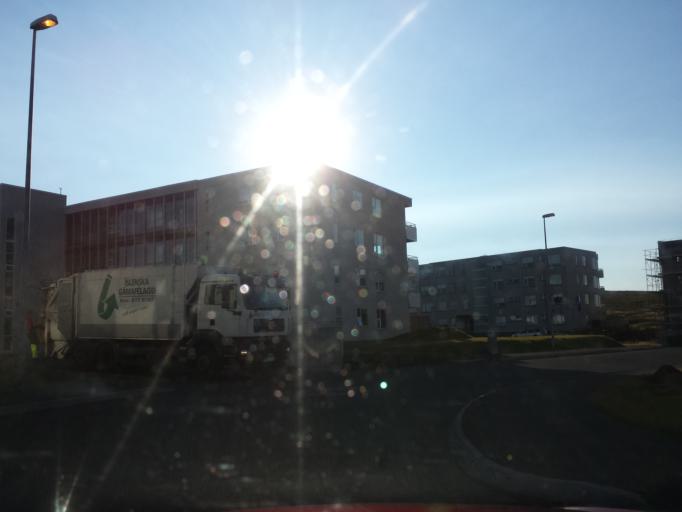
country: IS
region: Capital Region
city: Reykjavik
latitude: 64.0830
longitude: -21.8199
